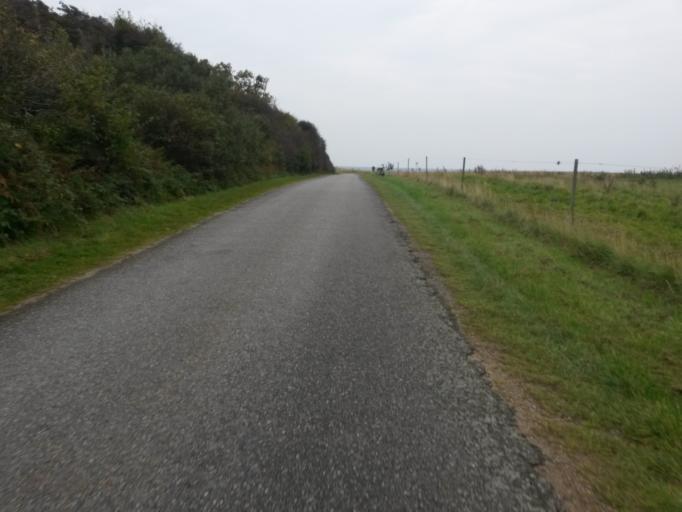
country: DK
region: South Denmark
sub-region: Langeland Kommune
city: Rudkobing
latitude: 54.7239
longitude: 10.6935
